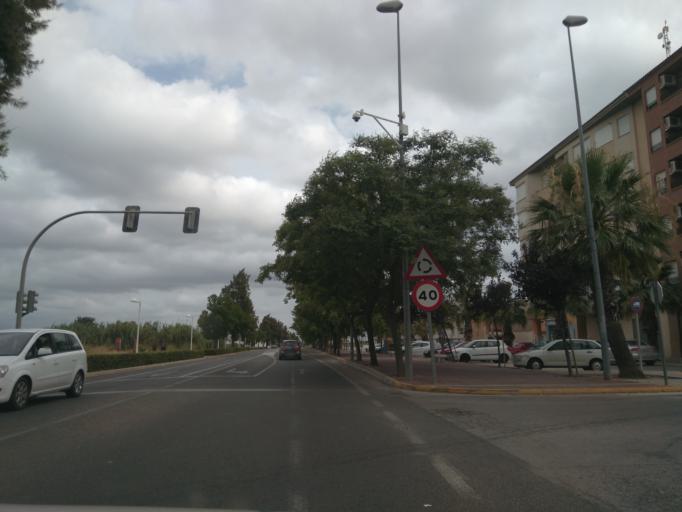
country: ES
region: Valencia
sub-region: Provincia de Valencia
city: Carlet
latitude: 39.2201
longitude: -0.5180
